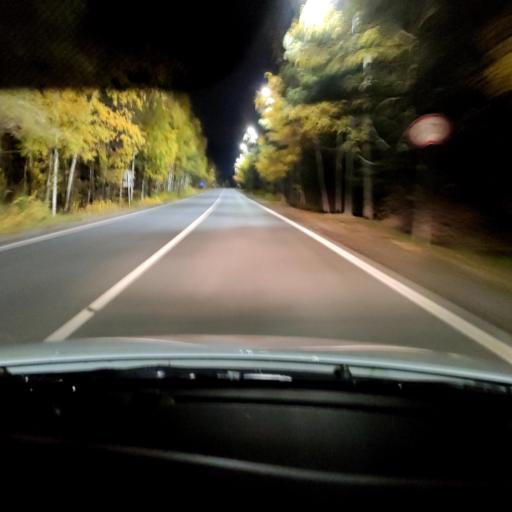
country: RU
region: Tatarstan
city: Verkhniy Uslon
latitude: 55.6371
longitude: 49.0223
